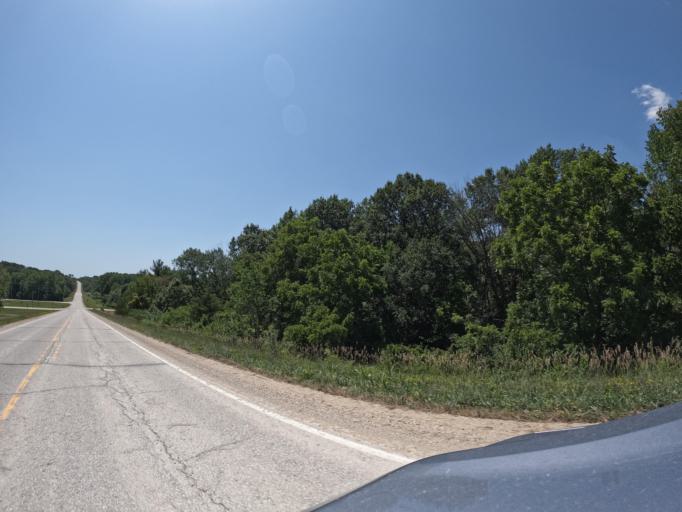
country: US
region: Iowa
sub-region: Henry County
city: Mount Pleasant
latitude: 40.9401
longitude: -91.6164
